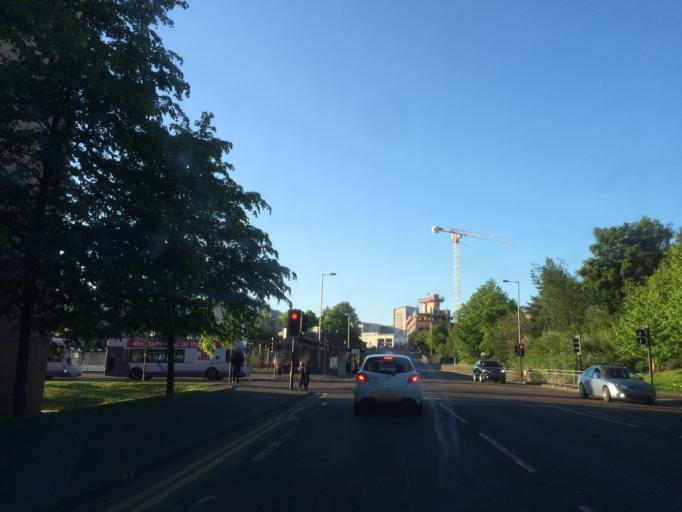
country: GB
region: Scotland
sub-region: Glasgow City
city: Glasgow
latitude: 55.8642
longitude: -4.2490
